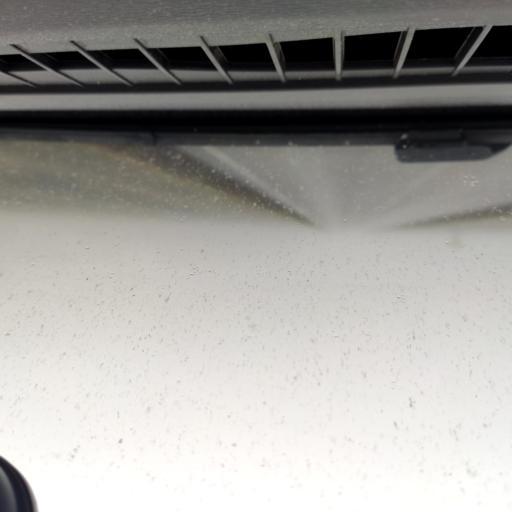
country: RU
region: Belgorod
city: Ilovka
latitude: 50.7548
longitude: 38.7233
